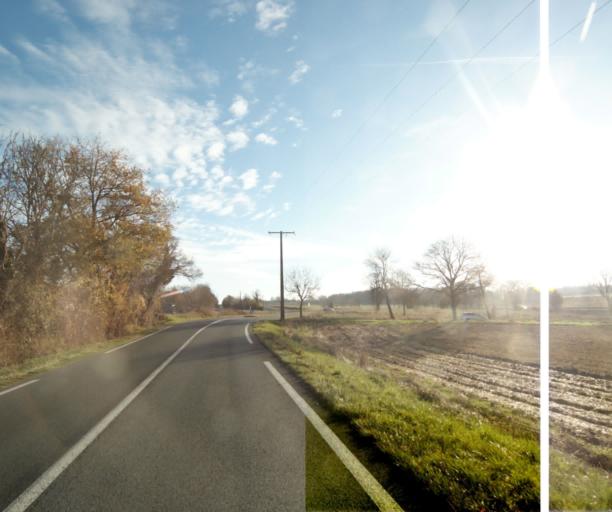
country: FR
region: Poitou-Charentes
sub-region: Departement de la Charente-Maritime
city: Saint-Georges-des-Coteaux
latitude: 45.7464
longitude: -0.6936
